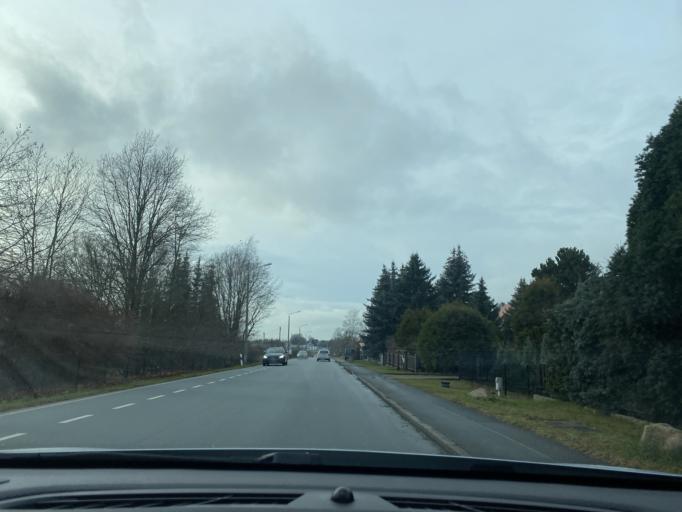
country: DE
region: Saxony
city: Goerlitz
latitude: 51.1476
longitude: 14.9395
